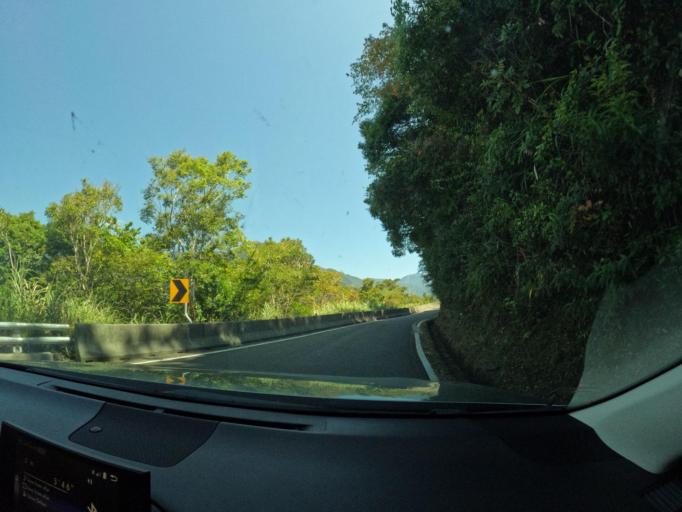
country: TW
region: Taiwan
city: Yujing
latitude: 23.2907
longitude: 120.8526
